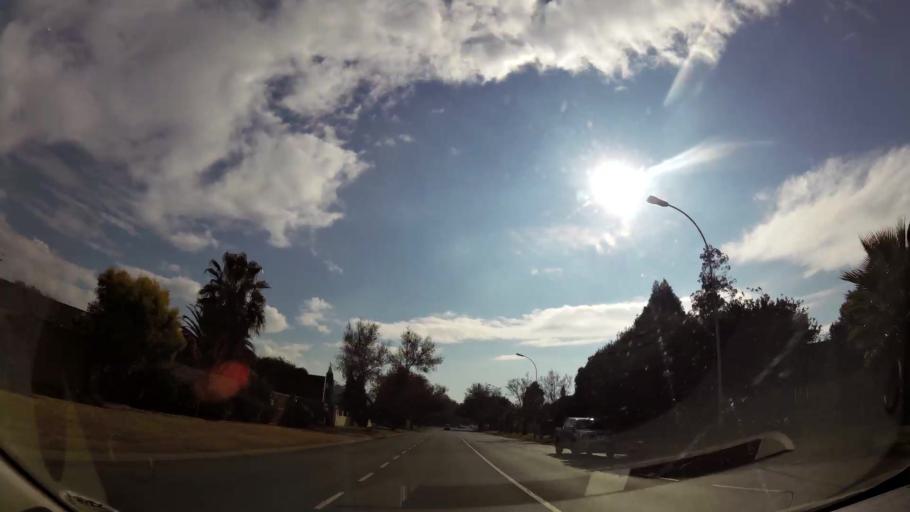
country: ZA
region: Gauteng
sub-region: Sedibeng District Municipality
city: Meyerton
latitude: -26.5535
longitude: 28.0323
